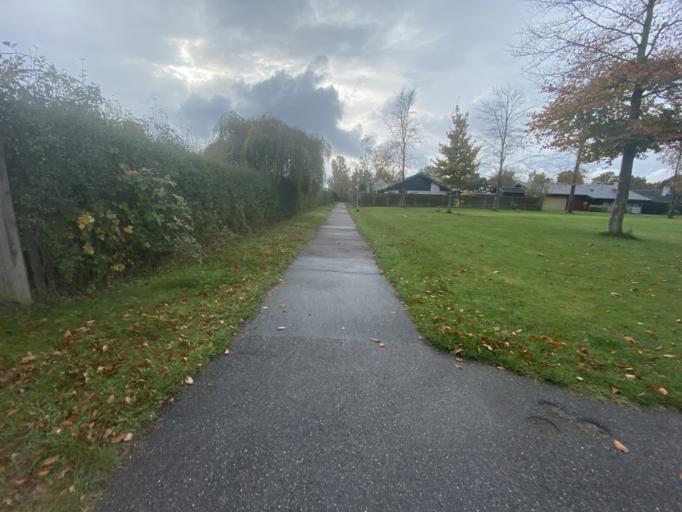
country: DK
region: Capital Region
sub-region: Dragor Kommune
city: Dragor
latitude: 55.5905
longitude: 12.6494
